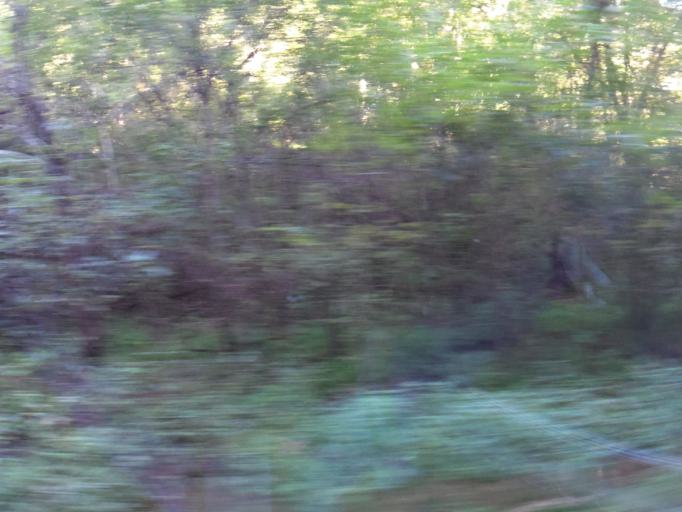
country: US
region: Tennessee
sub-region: Union County
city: Luttrell
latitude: 36.2195
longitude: -83.7397
